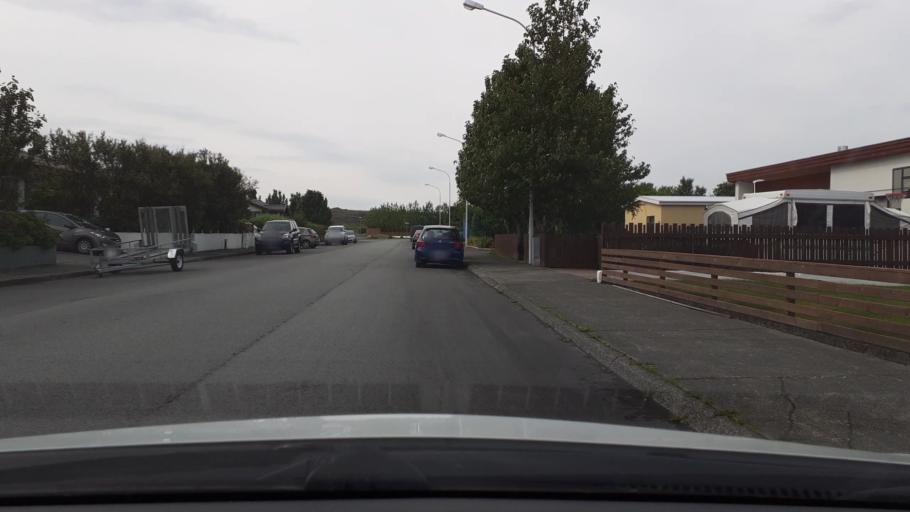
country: IS
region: Southern Peninsula
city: Reykjanesbaer
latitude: 63.9871
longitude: -22.5547
